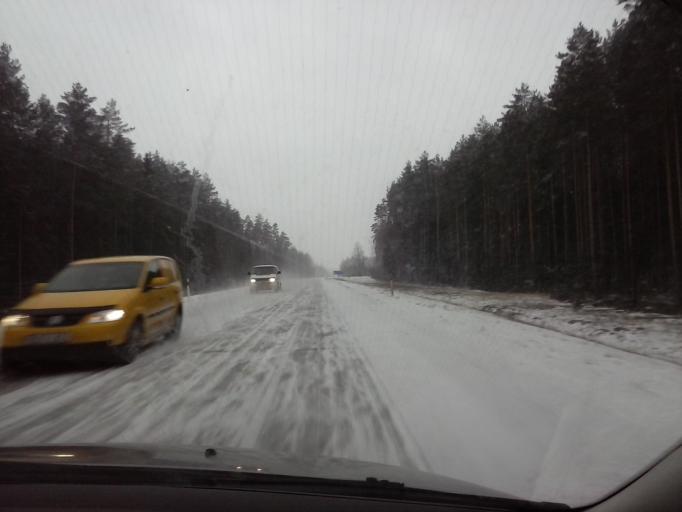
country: EE
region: Valgamaa
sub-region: Valga linn
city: Valga
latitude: 57.8640
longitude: 26.1446
